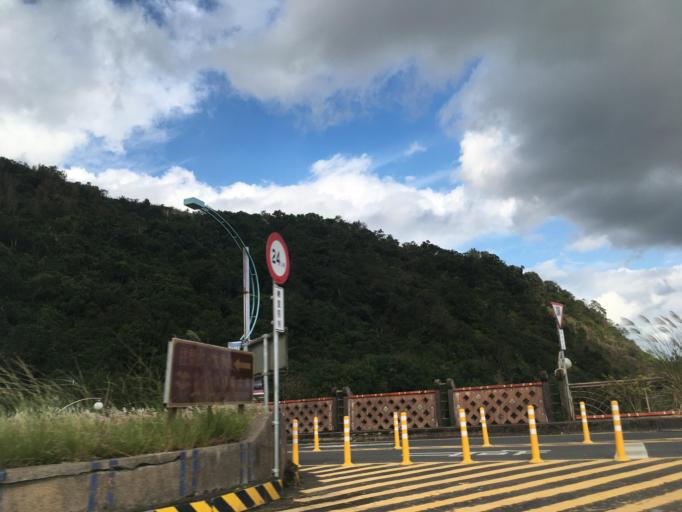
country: TW
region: Taiwan
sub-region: Yilan
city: Yilan
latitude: 24.6714
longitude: 121.6059
